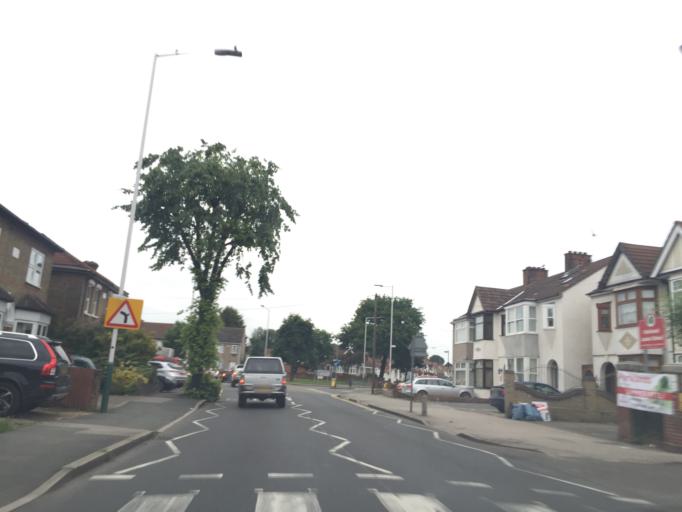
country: GB
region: England
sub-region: Greater London
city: Collier Row
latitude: 51.5884
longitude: 0.1718
